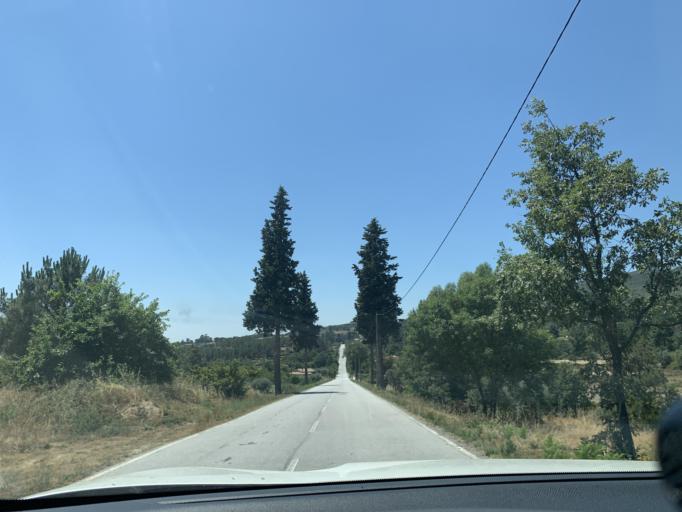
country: PT
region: Guarda
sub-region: Fornos de Algodres
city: Fornos de Algodres
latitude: 40.5813
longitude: -7.6272
